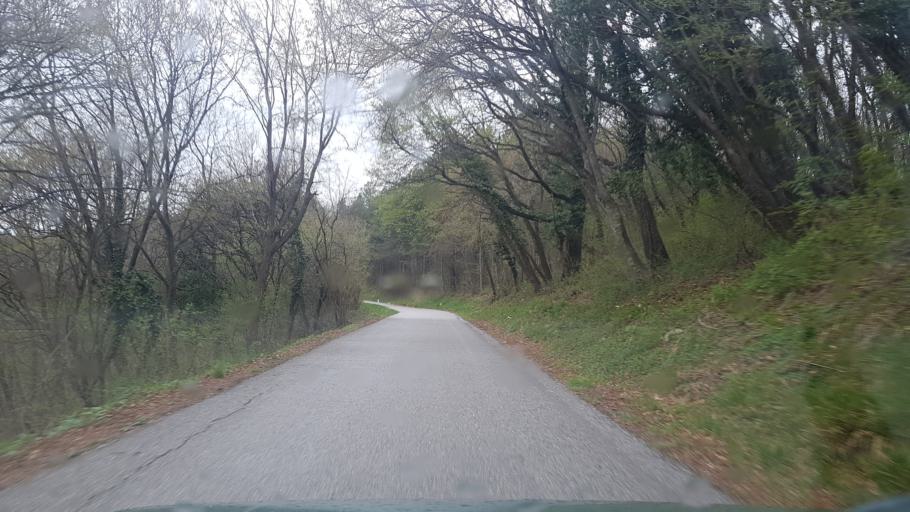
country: SI
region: Kanal
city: Deskle
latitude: 46.0572
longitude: 13.5643
